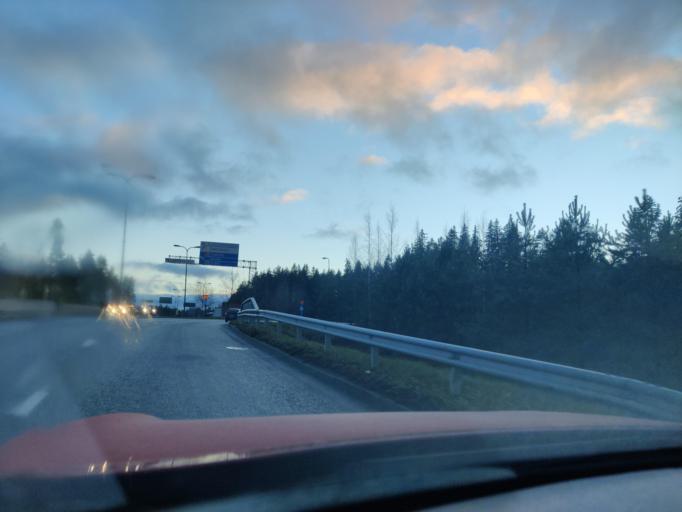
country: FI
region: Pirkanmaa
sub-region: Tampere
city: Nokia
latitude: 61.4696
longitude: 23.5039
